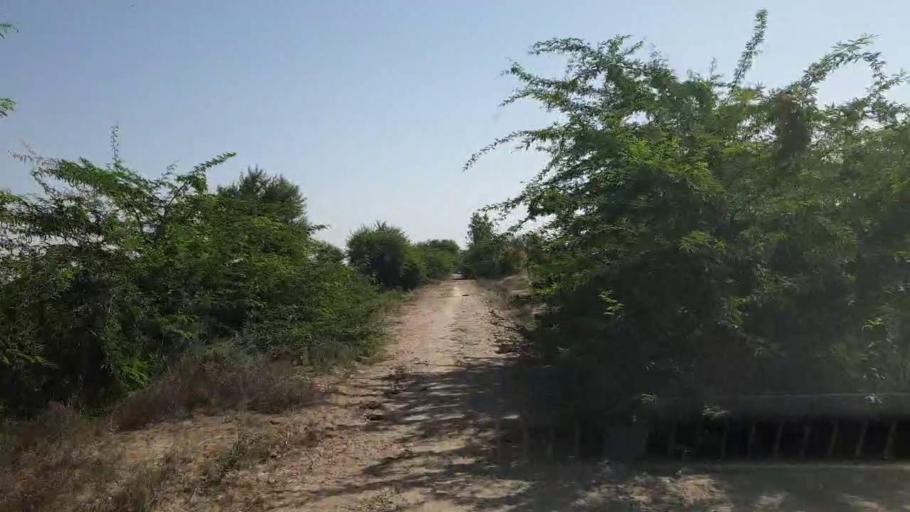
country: PK
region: Sindh
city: Kadhan
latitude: 24.5940
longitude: 69.0065
